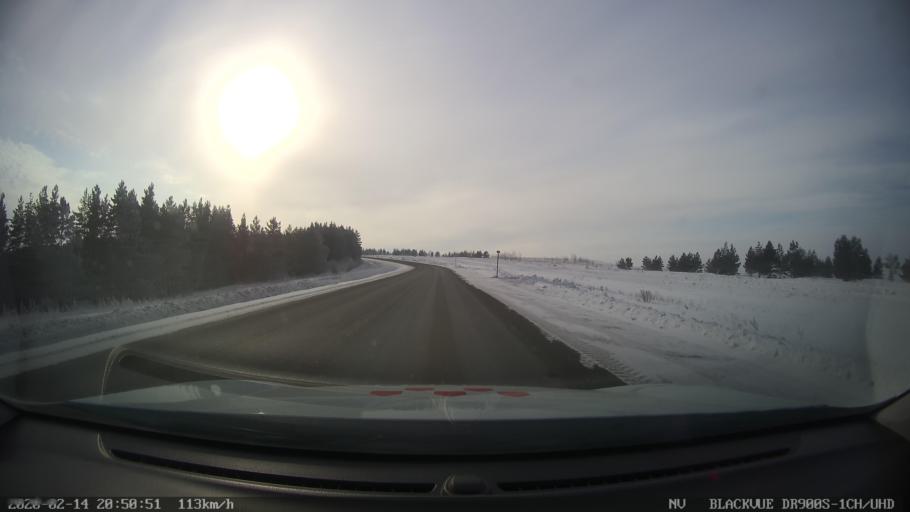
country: RU
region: Tatarstan
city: Kuybyshevskiy Zaton
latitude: 55.2207
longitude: 49.2320
